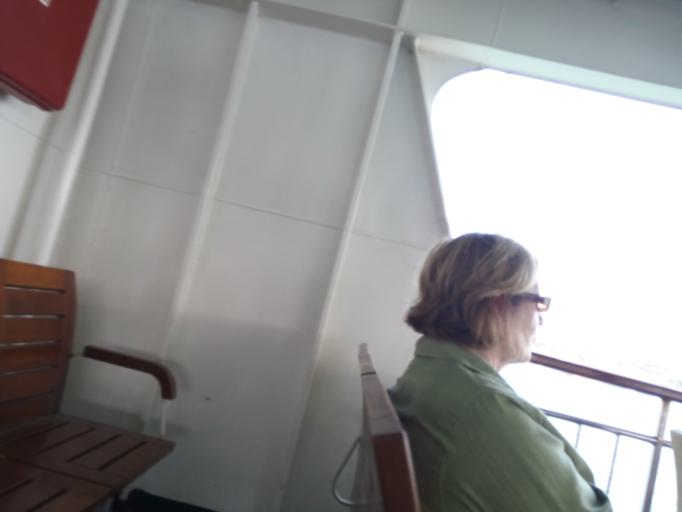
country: TR
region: Istanbul
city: UEskuedar
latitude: 41.0383
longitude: 29.0155
